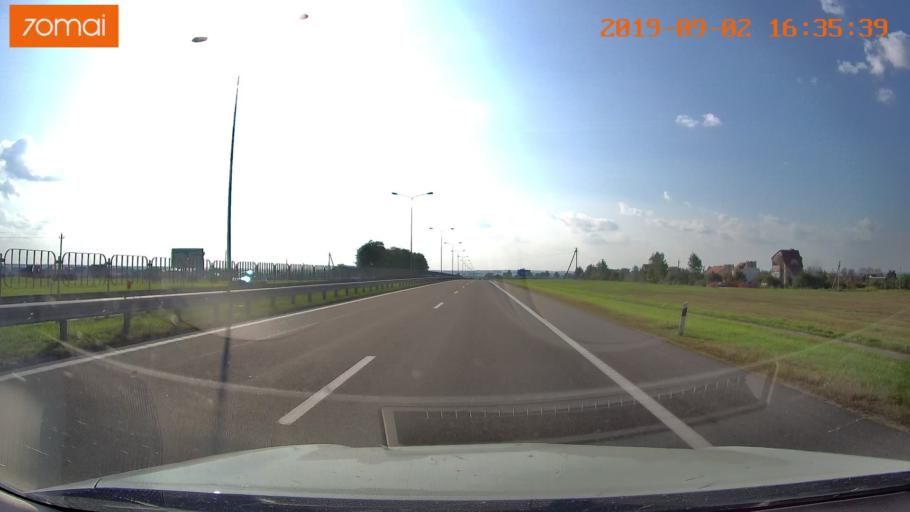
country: BY
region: Minsk
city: Smilavichy
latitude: 53.7597
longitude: 27.9995
